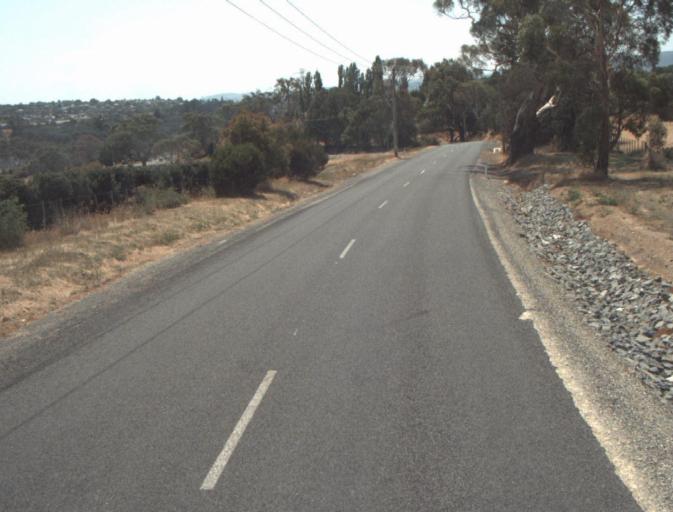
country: AU
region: Tasmania
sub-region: Launceston
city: Newstead
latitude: -41.4793
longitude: 147.1901
